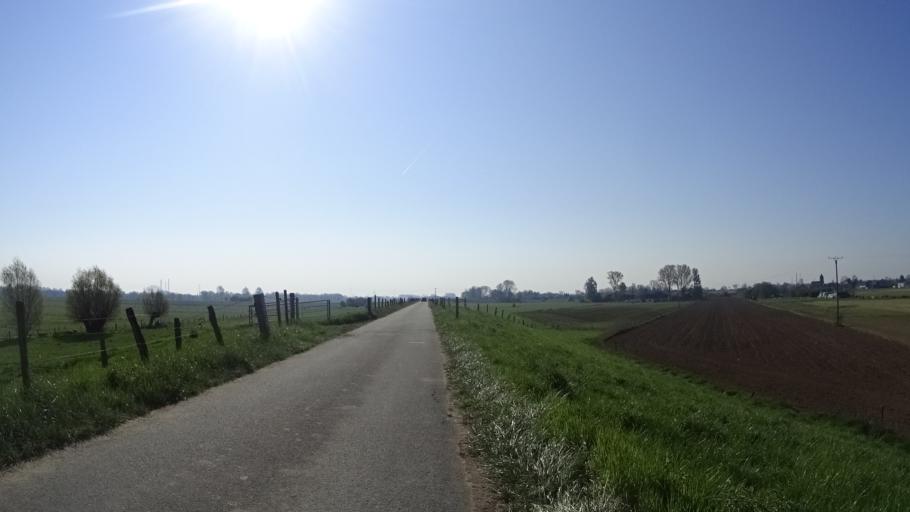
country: DE
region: North Rhine-Westphalia
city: Rheinberg
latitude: 51.6031
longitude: 6.5770
